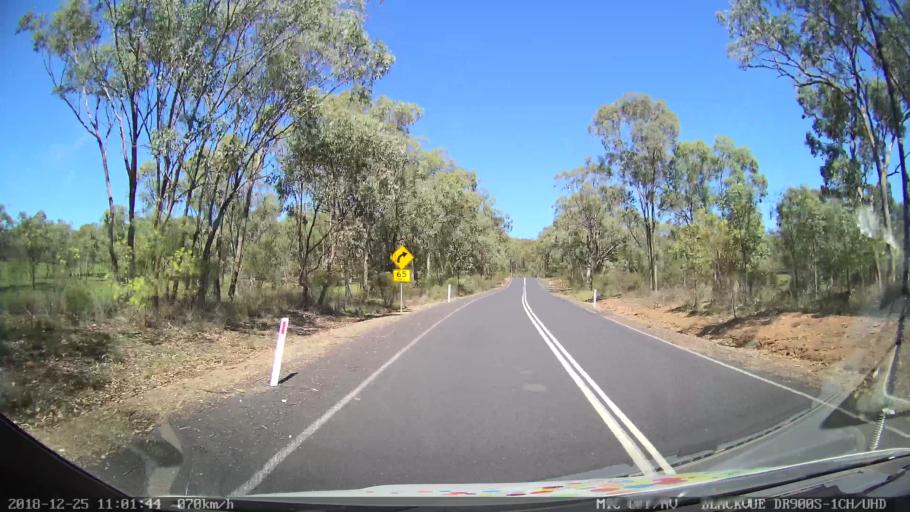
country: AU
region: New South Wales
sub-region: Upper Hunter Shire
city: Merriwa
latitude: -32.4061
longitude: 150.1983
